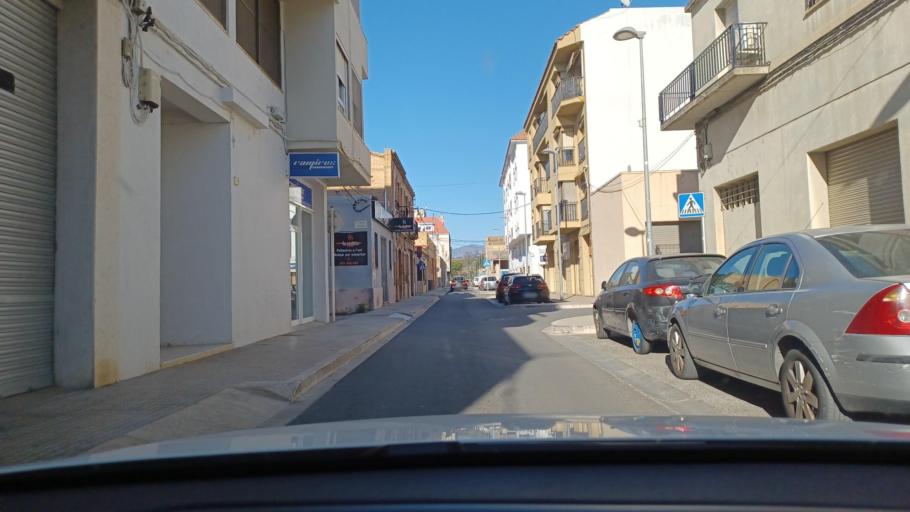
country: ES
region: Catalonia
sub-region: Provincia de Tarragona
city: Tortosa
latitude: 40.8179
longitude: 0.5232
